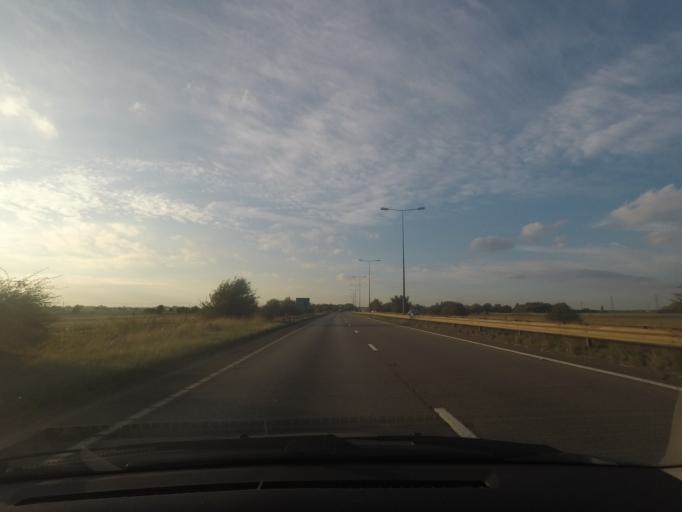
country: GB
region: England
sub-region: North East Lincolnshire
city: Healing
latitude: 53.5854
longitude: -0.1493
